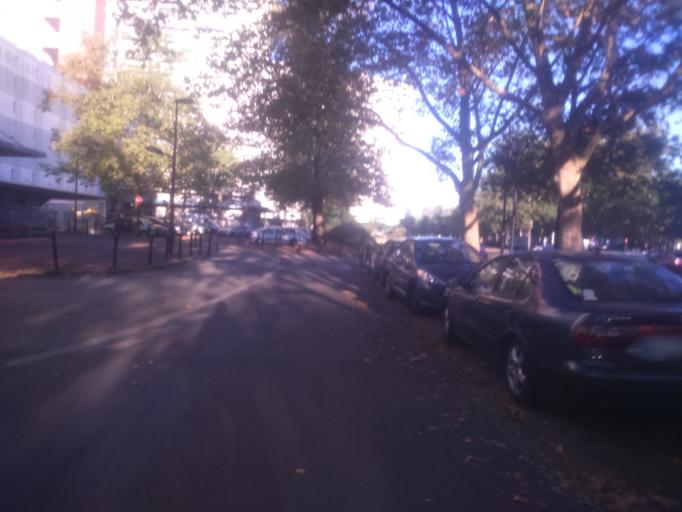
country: FR
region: Aquitaine
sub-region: Departement de la Gironde
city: Le Bouscat
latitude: 44.8737
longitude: -0.5705
